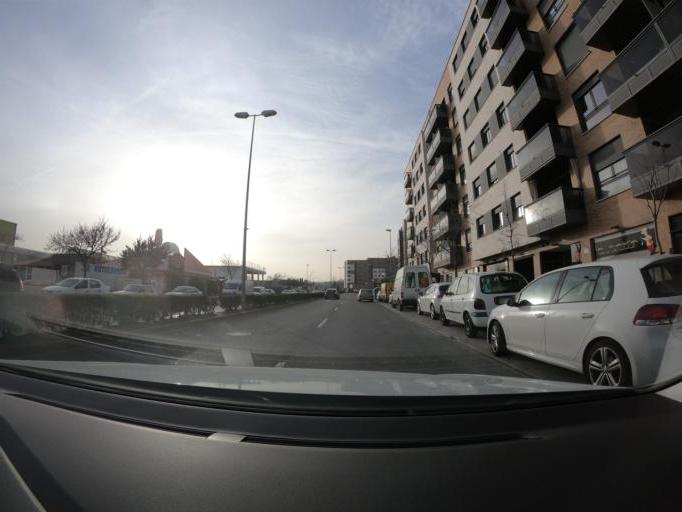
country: ES
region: La Rioja
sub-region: Provincia de La Rioja
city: Logrono
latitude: 42.4536
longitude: -2.4642
